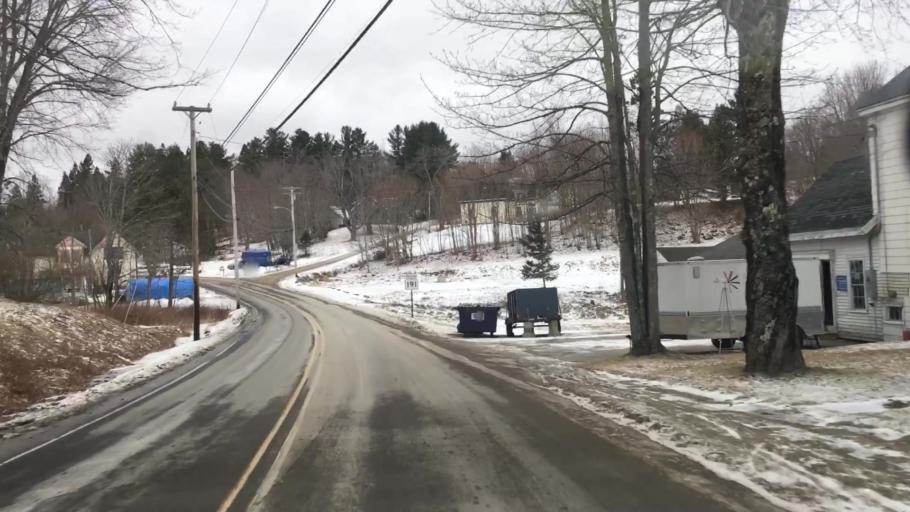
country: US
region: Maine
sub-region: Washington County
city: East Machias
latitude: 44.7322
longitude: -67.3905
